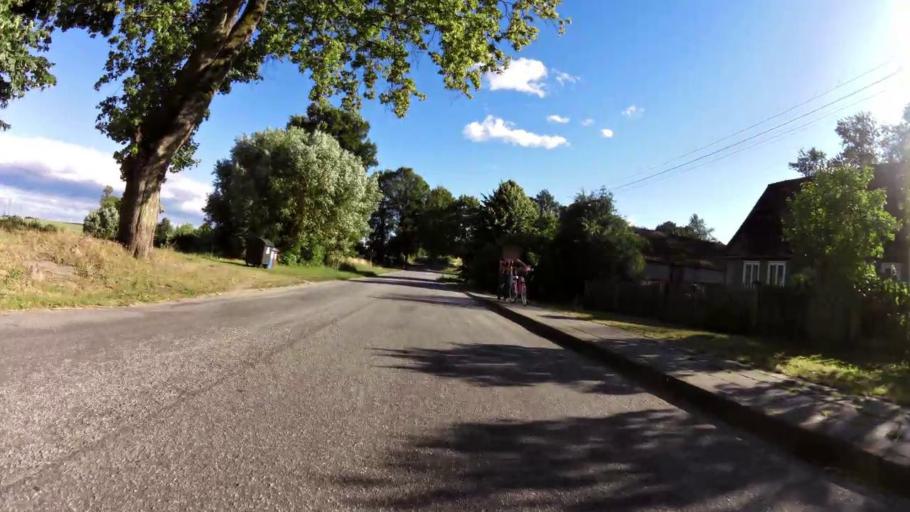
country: PL
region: West Pomeranian Voivodeship
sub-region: Powiat swidwinski
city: Swidwin
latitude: 53.7570
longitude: 15.6927
